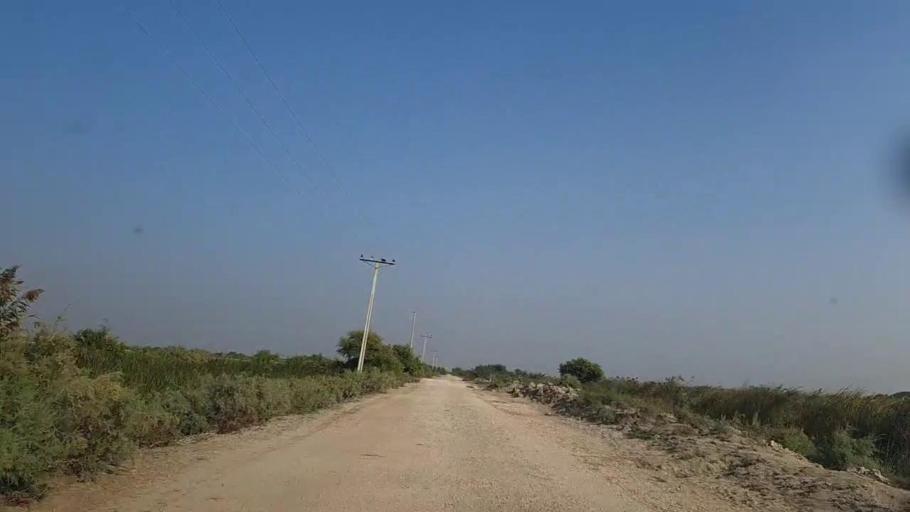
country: PK
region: Sindh
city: Jati
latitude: 24.4602
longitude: 68.2997
